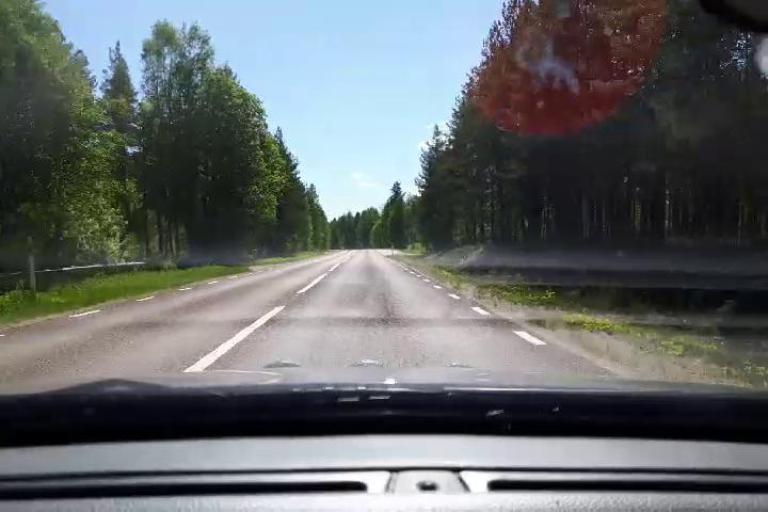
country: SE
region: Jaemtland
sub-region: Harjedalens Kommun
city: Sveg
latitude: 62.1529
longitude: 14.9536
